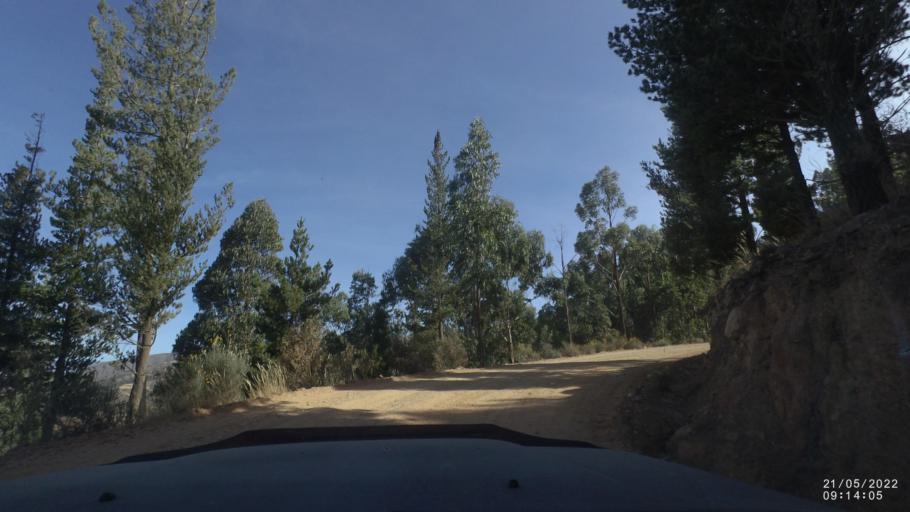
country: BO
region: Cochabamba
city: Cochabamba
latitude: -17.3661
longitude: -66.0289
